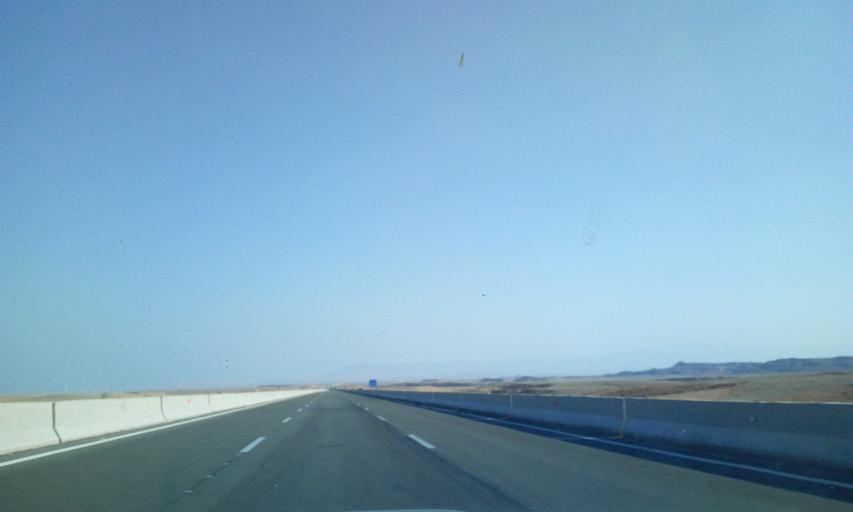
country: EG
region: As Suways
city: Ain Sukhna
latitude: 29.2448
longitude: 32.4807
